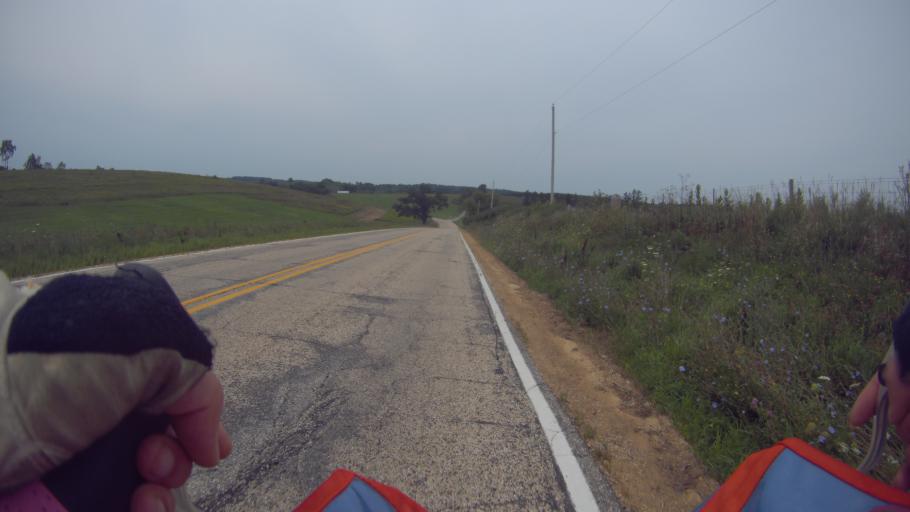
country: US
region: Wisconsin
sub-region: Dane County
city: Mount Horeb
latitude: 42.9379
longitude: -89.6700
